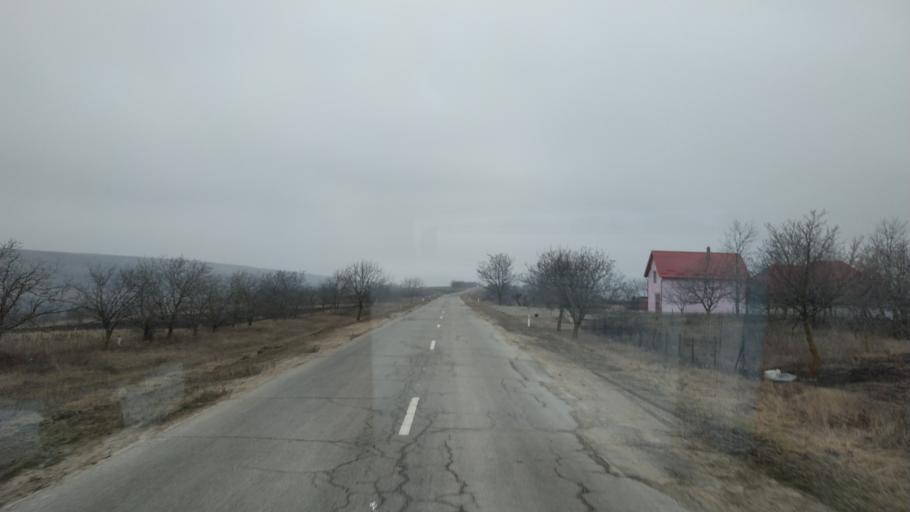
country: MD
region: Stinga Nistrului
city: Bucovat
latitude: 47.0240
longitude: 28.4255
